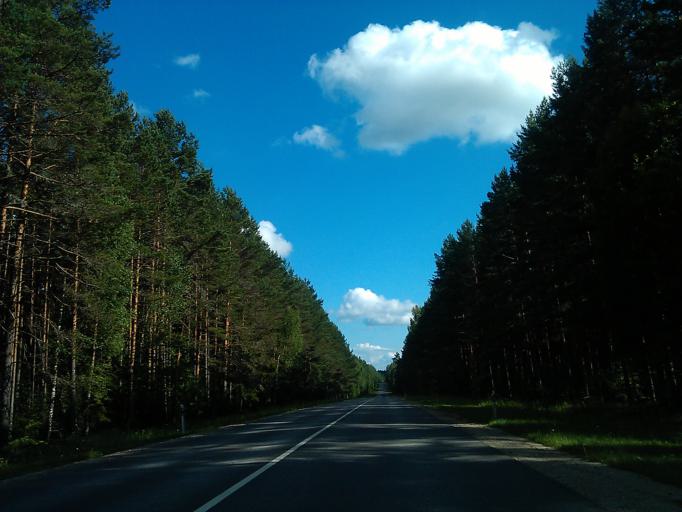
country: LV
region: Naukseni
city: Naukseni
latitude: 57.8099
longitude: 25.4073
